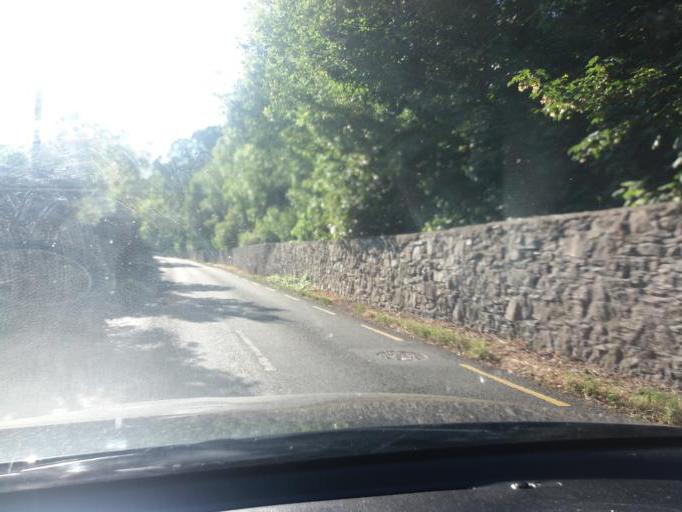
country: IE
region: Leinster
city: Lucan
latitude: 53.3682
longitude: -6.4298
